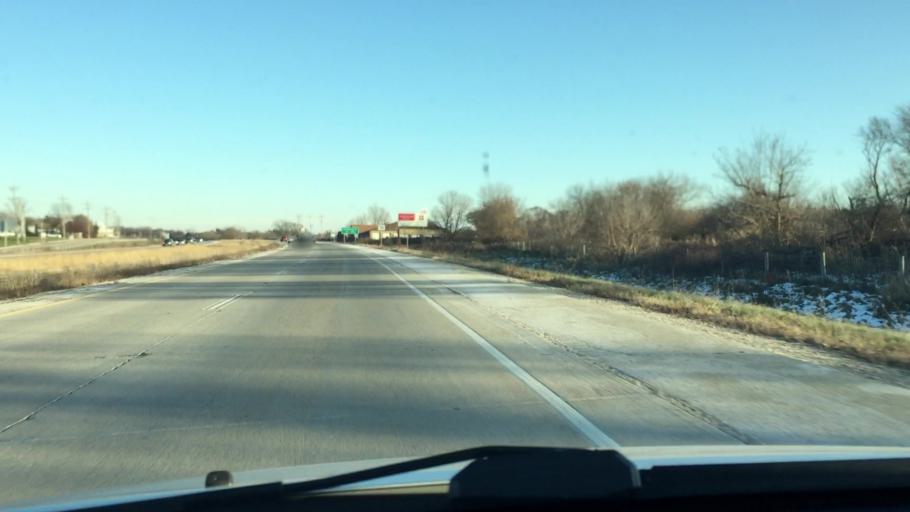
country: US
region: Wisconsin
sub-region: Waukesha County
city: Nashotah
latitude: 43.1038
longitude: -88.4227
